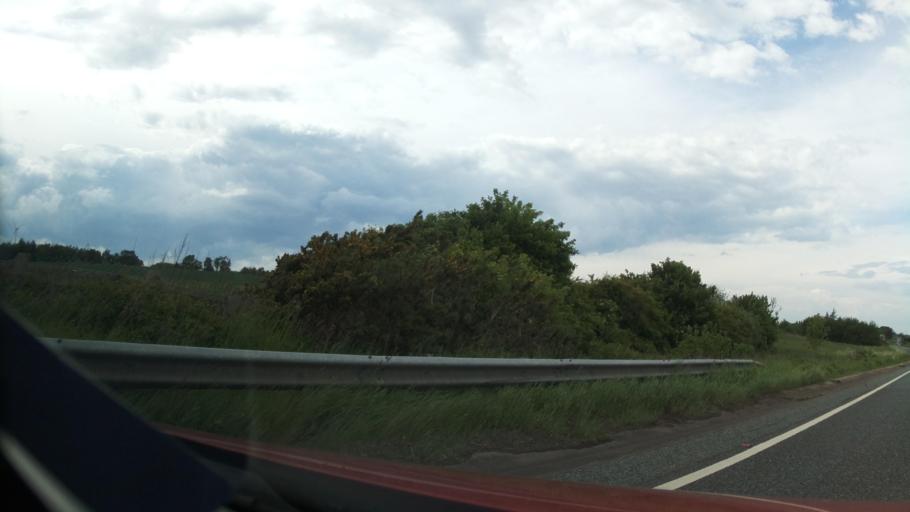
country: GB
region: England
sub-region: Northumberland
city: Ellingham
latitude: 55.5173
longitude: -1.7447
